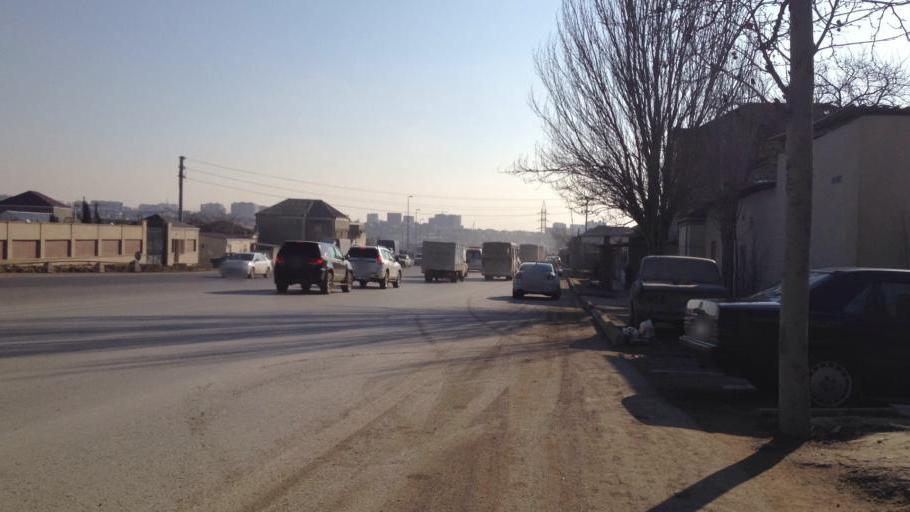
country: AZ
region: Baki
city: Sabuncu
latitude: 40.4438
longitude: 49.9337
